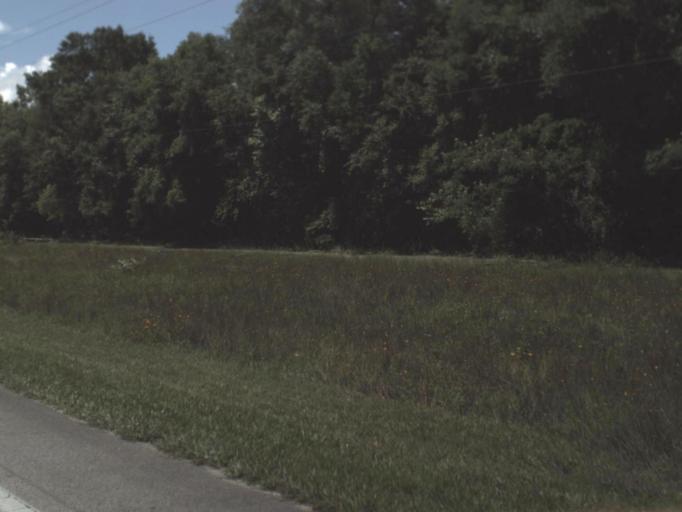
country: US
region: Florida
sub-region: Putnam County
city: Palatka
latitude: 29.5160
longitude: -81.6162
